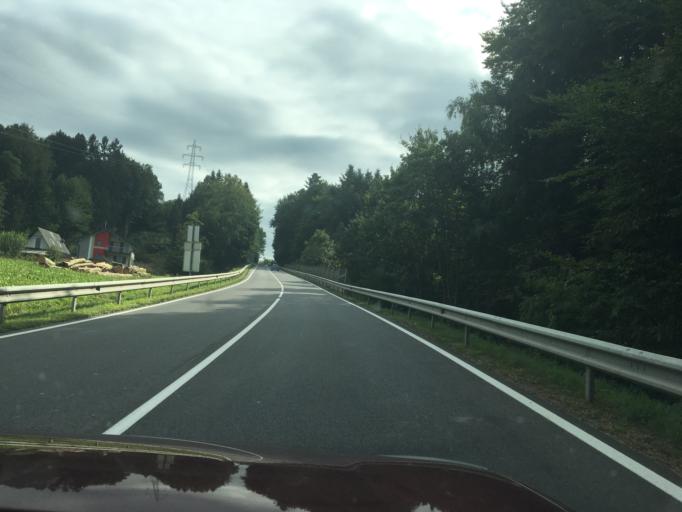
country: AT
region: Styria
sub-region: Politischer Bezirk Deutschlandsberg
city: Deutschlandsberg
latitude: 46.8109
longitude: 15.2275
